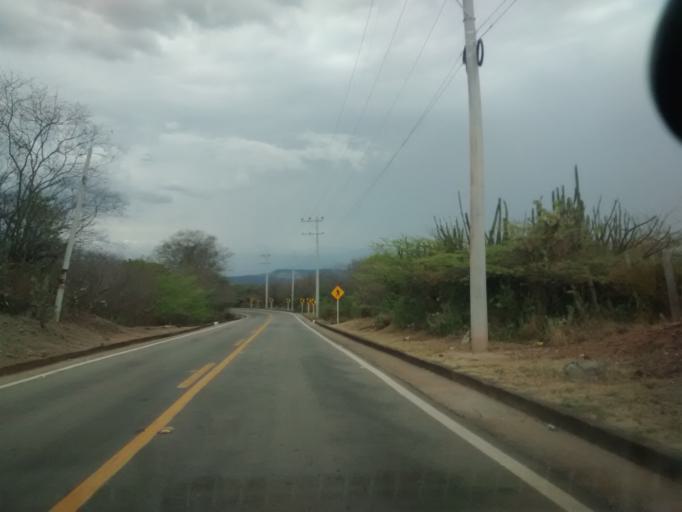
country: CO
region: Cundinamarca
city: Agua de Dios
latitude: 4.4279
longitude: -74.6933
